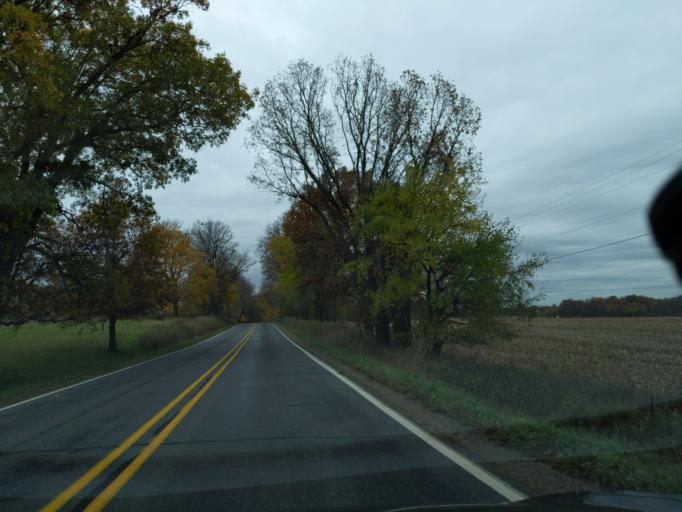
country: US
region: Michigan
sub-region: Jackson County
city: Spring Arbor
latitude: 42.2907
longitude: -84.6002
